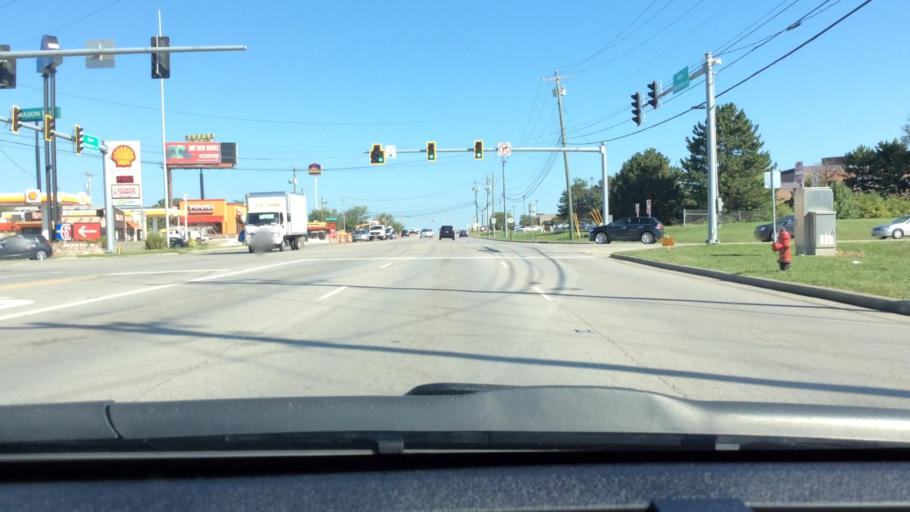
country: US
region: Ohio
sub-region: Hamilton County
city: Sixteen Mile Stand
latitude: 39.2948
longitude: -84.3153
